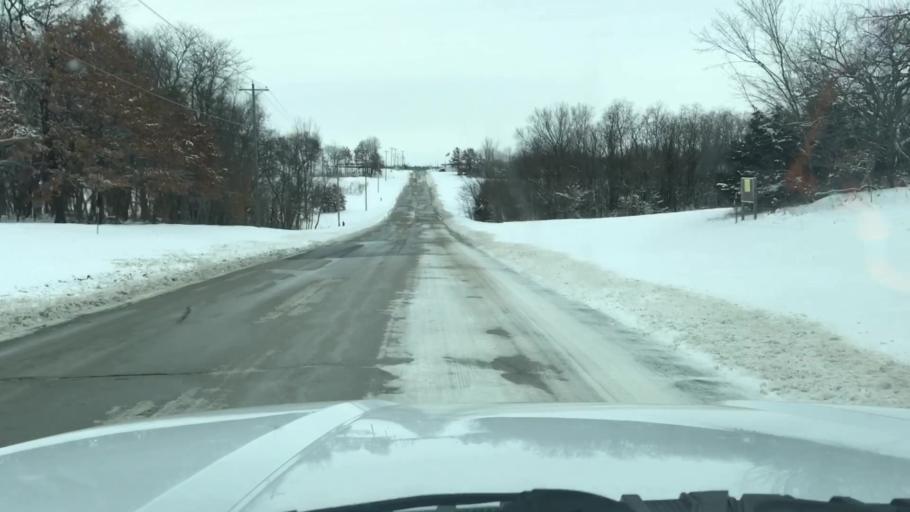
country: US
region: Missouri
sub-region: Clinton County
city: Cameron
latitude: 39.7458
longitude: -94.2153
